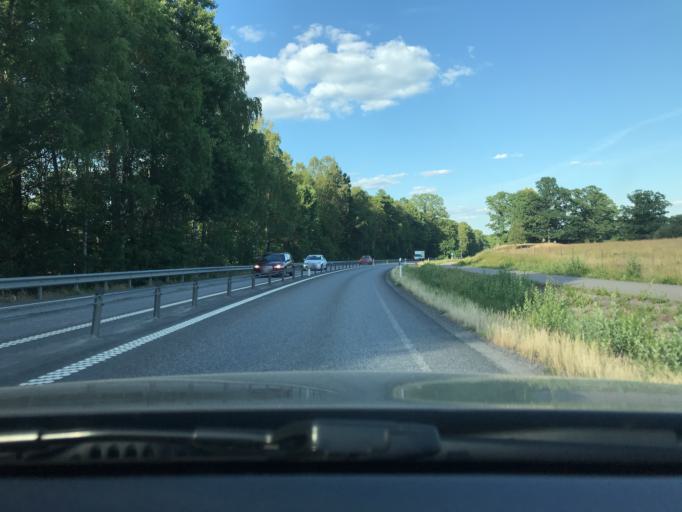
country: SE
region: Kronoberg
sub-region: Vaxjo Kommun
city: Rottne
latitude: 56.9394
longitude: 14.8711
